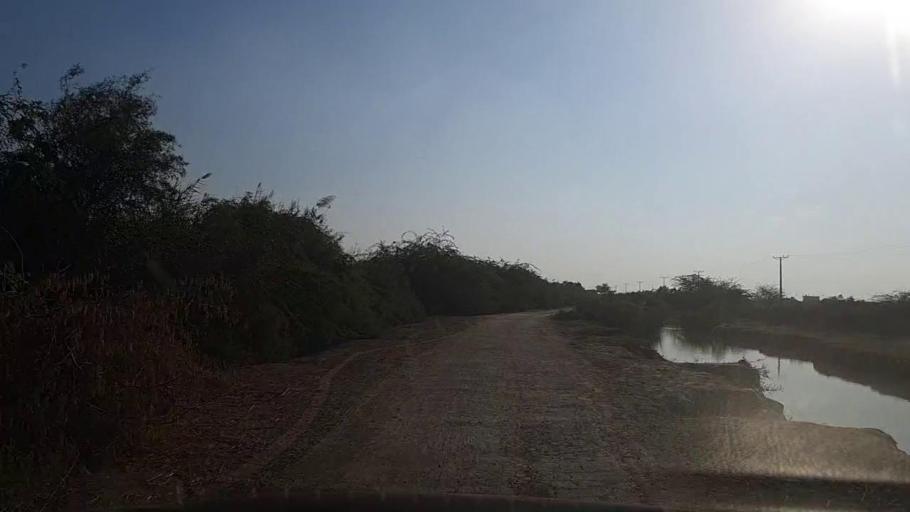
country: PK
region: Sindh
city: Gharo
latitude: 24.7104
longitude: 67.6836
